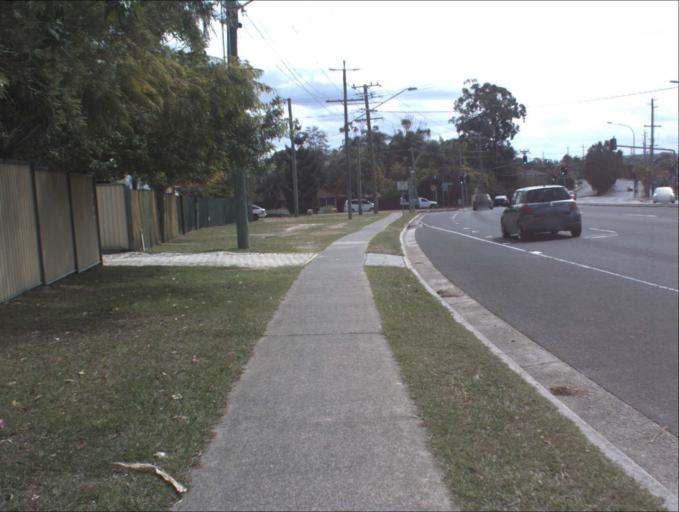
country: AU
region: Queensland
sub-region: Logan
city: Logan Reserve
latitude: -27.6811
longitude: 153.0898
